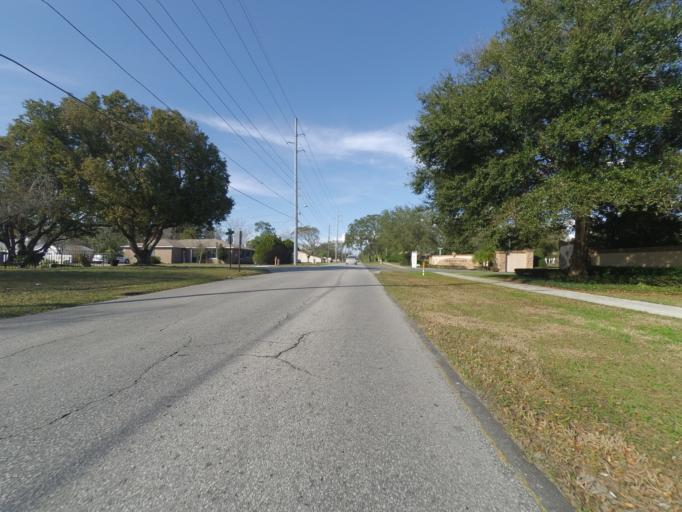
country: US
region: Florida
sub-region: Lake County
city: Eustis
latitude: 28.8331
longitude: -81.6835
